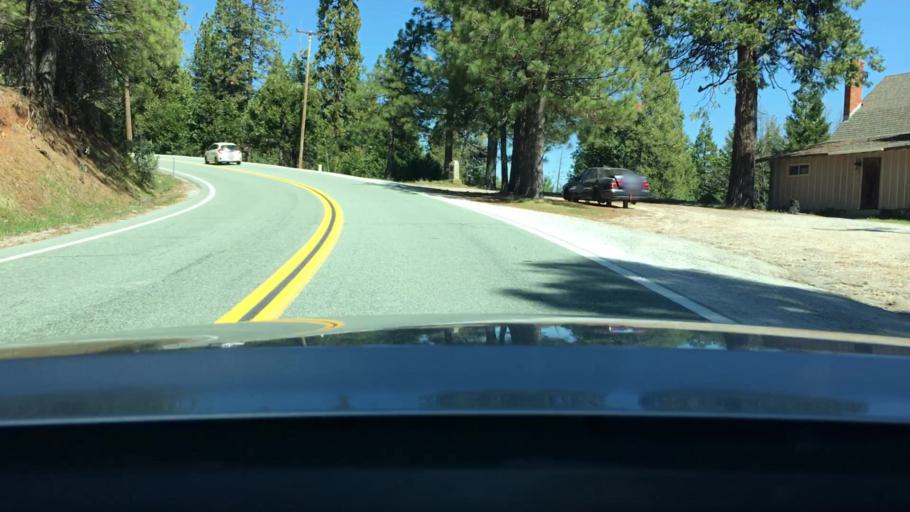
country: US
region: California
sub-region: Amador County
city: Pioneer
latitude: 38.4705
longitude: -120.5270
